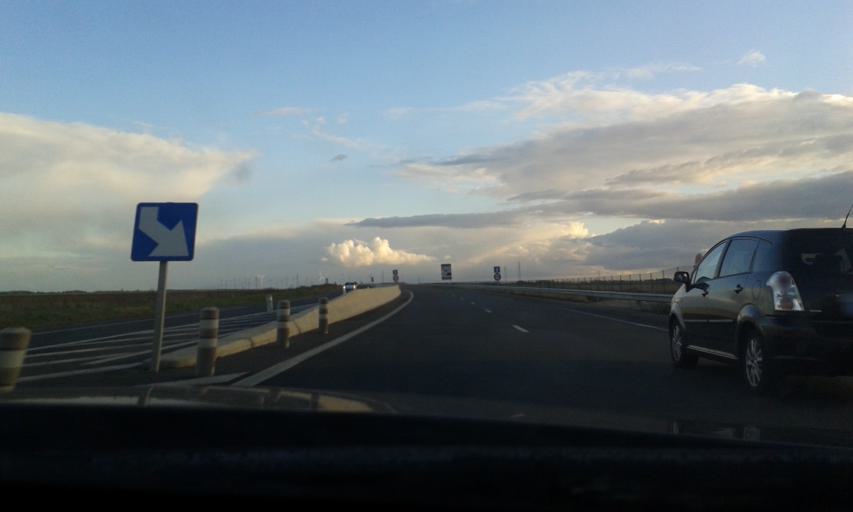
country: FR
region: Centre
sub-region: Departement d'Eure-et-Loir
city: Sours
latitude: 48.3737
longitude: 1.5884
